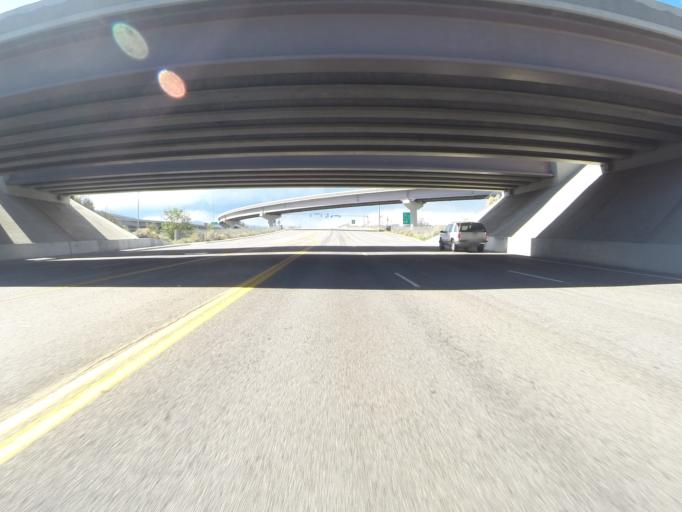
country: US
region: Utah
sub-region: Salt Lake County
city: South Salt Lake
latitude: 40.7255
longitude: -111.9050
